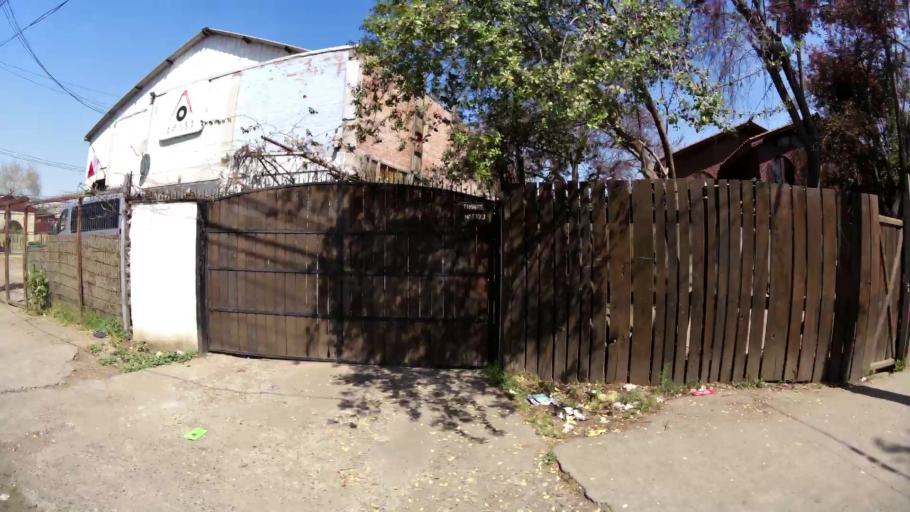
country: CL
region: Santiago Metropolitan
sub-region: Provincia de Santiago
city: Lo Prado
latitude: -33.3690
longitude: -70.7143
